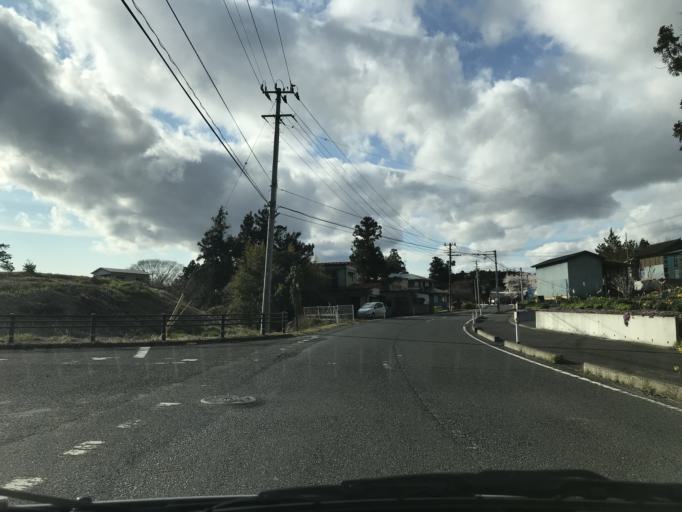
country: JP
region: Miyagi
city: Wakuya
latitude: 38.6218
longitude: 141.2263
